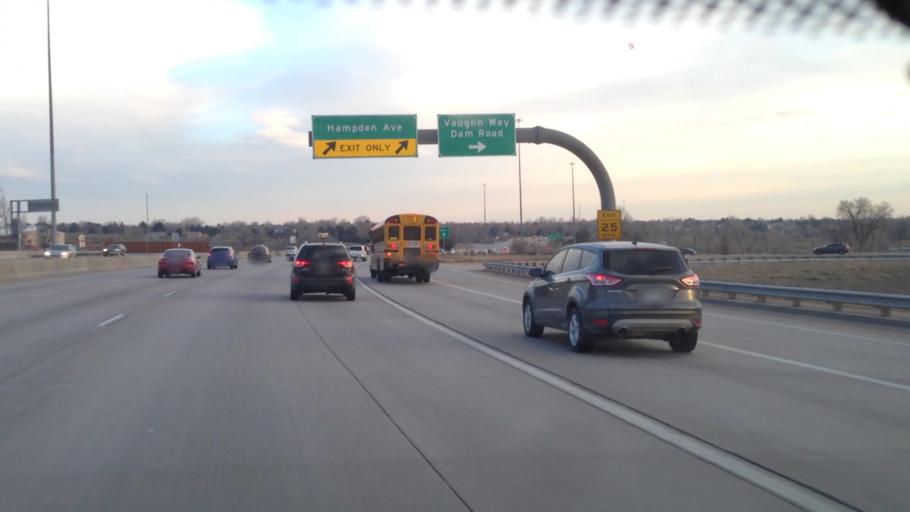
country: US
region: Colorado
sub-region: Adams County
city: Aurora
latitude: 39.6567
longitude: -104.8366
